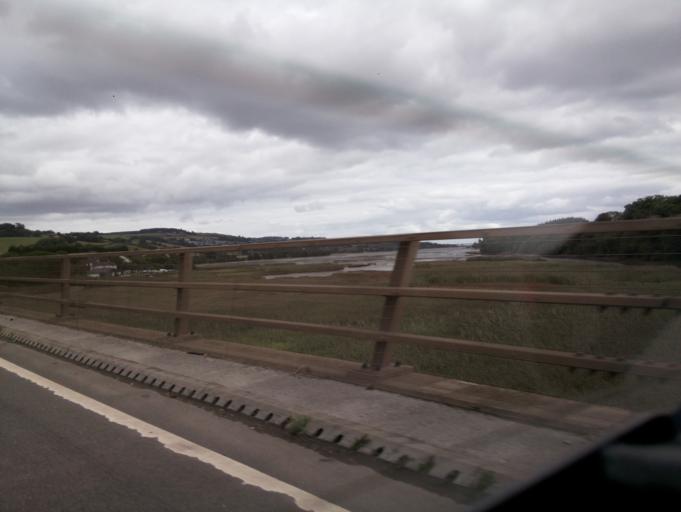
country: GB
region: England
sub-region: Devon
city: Kingsteignton
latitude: 50.5378
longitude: -3.5862
